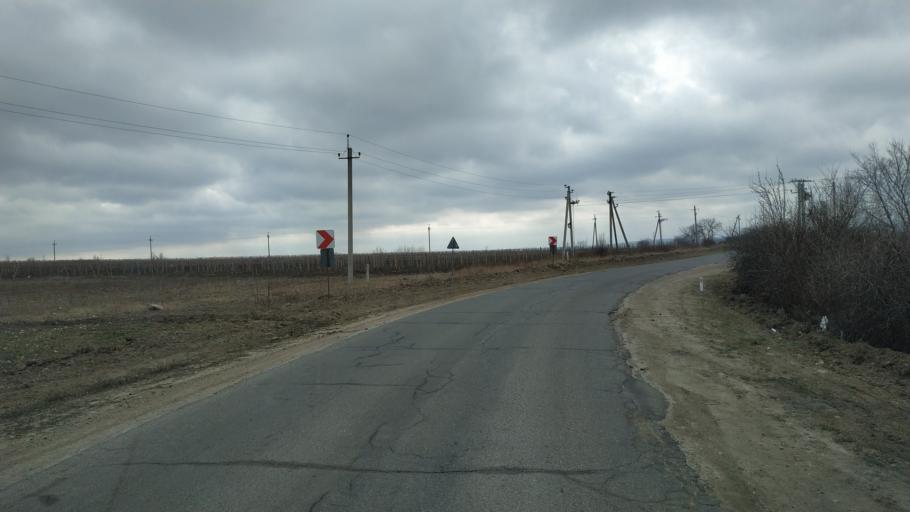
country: MD
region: Laloveni
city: Ialoveni
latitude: 46.9046
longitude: 28.7769
